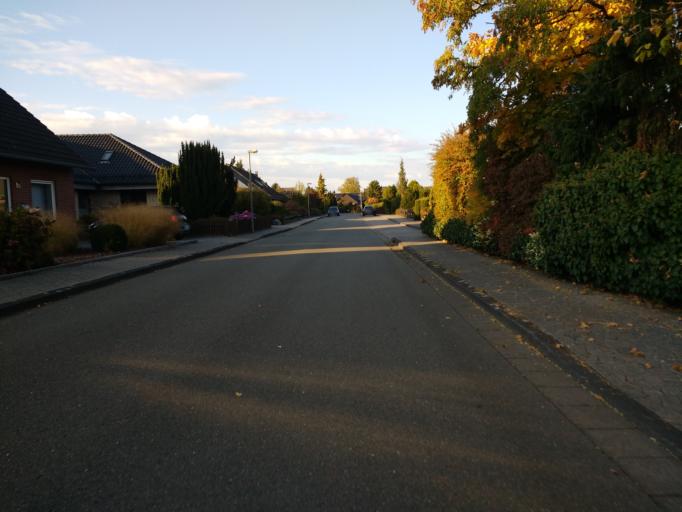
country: DE
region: Lower Saxony
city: Gifhorn
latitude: 52.4711
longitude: 10.5707
